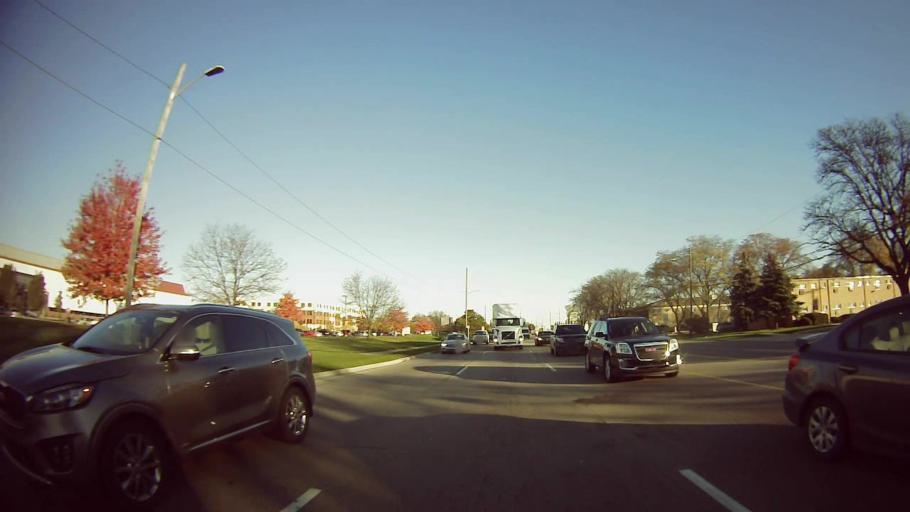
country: US
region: Michigan
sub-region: Macomb County
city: Center Line
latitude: 42.5002
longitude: -83.0282
